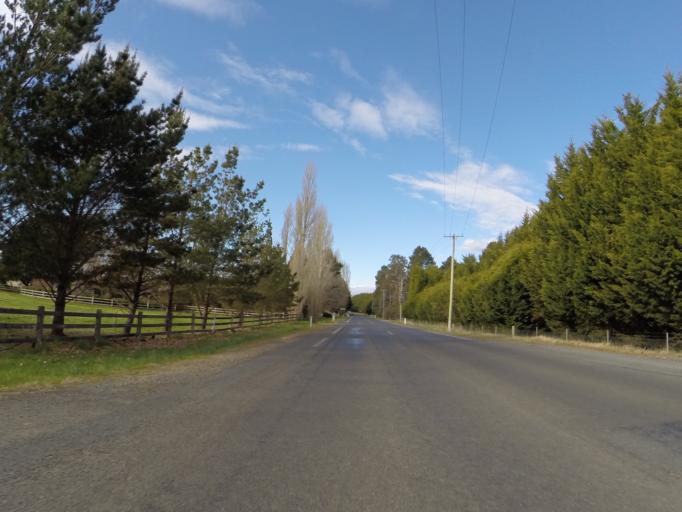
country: AU
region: New South Wales
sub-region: Wingecarribee
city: Moss Vale
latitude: -34.5789
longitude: 150.3053
